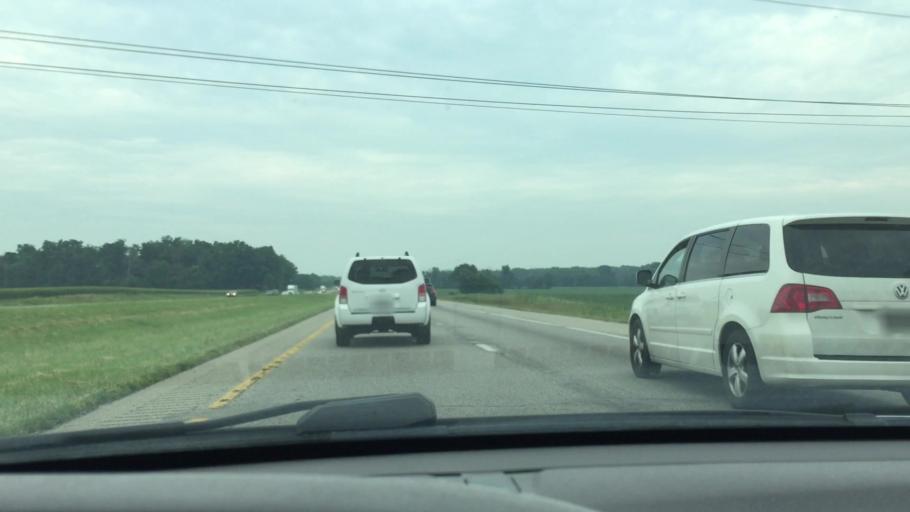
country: US
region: Ohio
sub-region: Warren County
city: Waynesville
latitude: 39.4664
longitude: -83.9783
